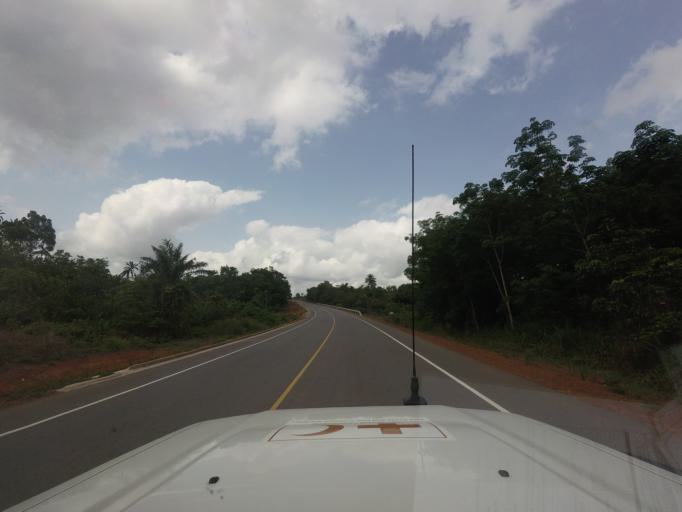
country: LR
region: Nimba
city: Sanniquellie
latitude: 7.1708
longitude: -9.0359
